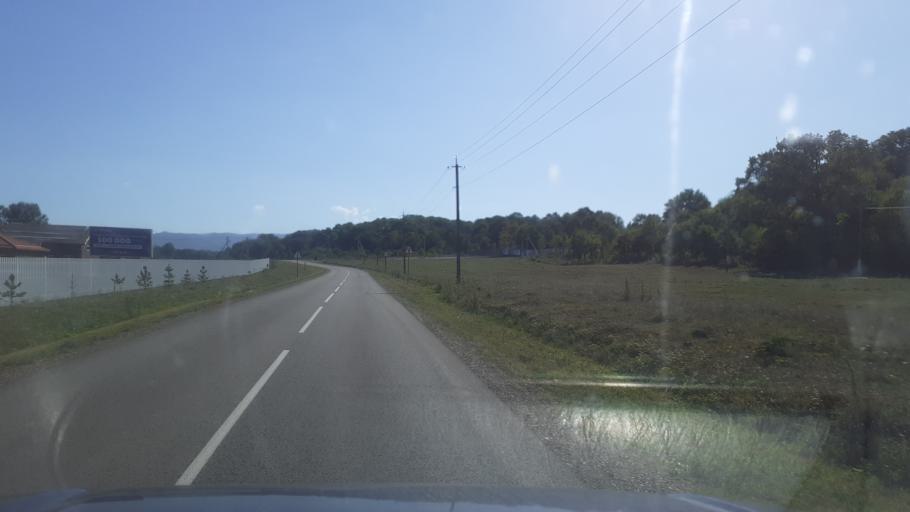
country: RU
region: Krasnodarskiy
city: Azovskaya
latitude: 44.7710
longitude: 38.5733
